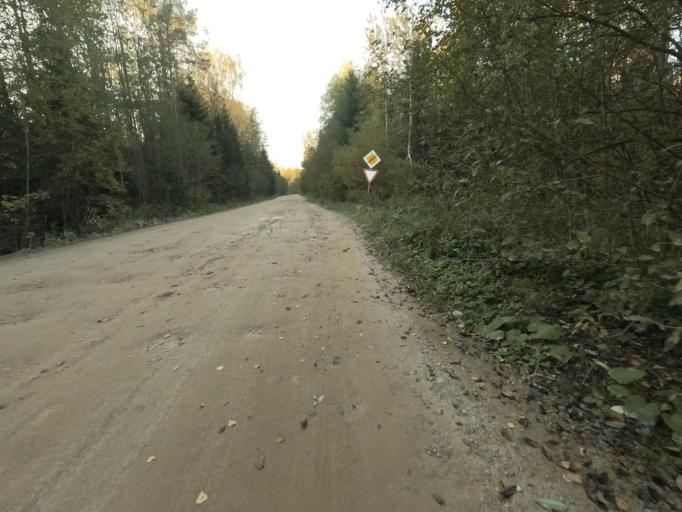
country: RU
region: Leningrad
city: Lyuban'
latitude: 59.0143
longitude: 31.0870
